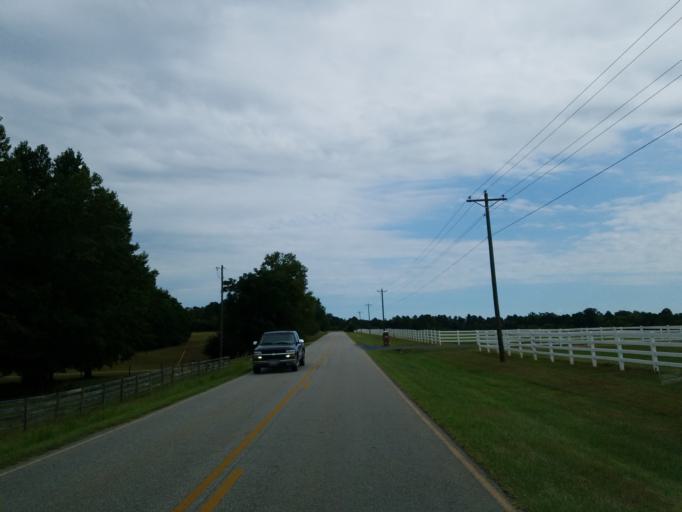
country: US
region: Georgia
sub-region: Monroe County
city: Forsyth
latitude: 32.9249
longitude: -83.9231
